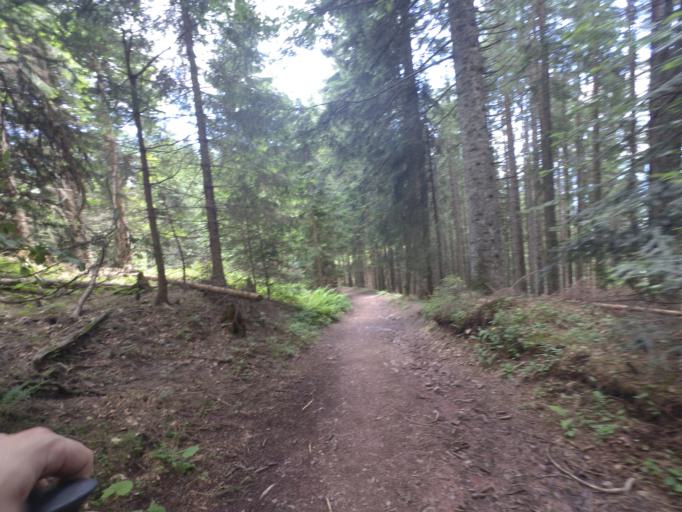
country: AT
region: Salzburg
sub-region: Politischer Bezirk Zell am See
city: Leogang
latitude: 47.4554
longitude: 12.7699
